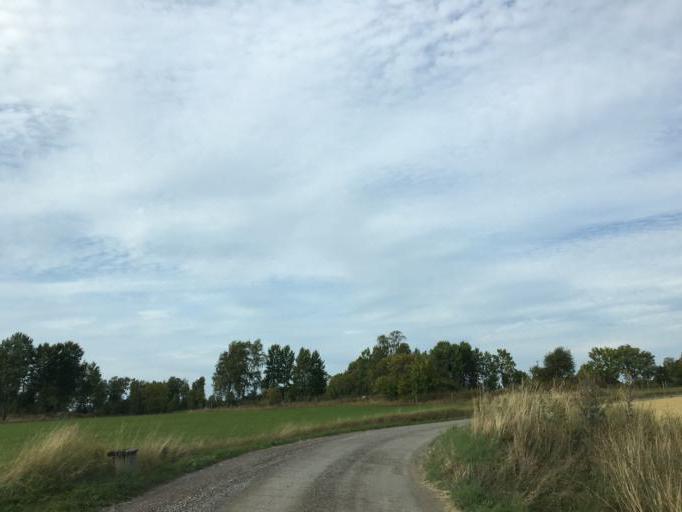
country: SE
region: Soedermanland
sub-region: Eskilstuna Kommun
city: Eskilstuna
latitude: 59.4070
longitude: 16.5095
